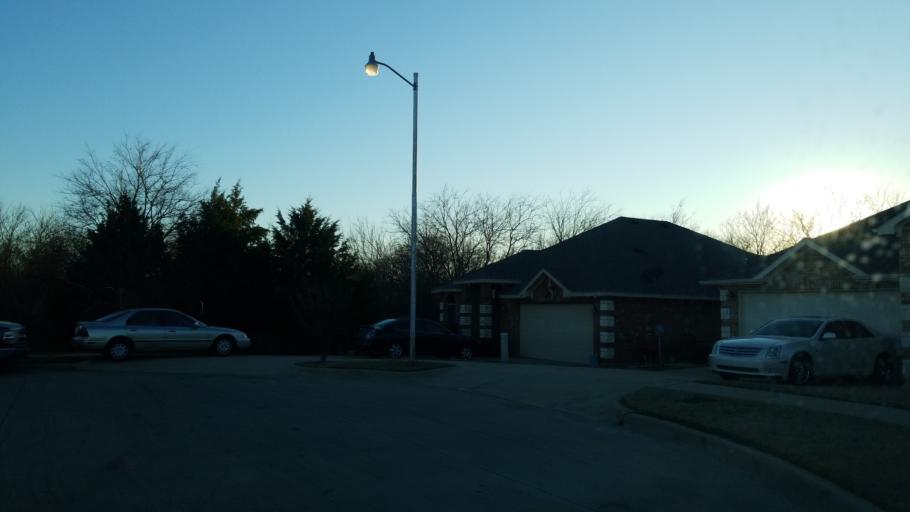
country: US
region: Texas
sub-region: Tarrant County
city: Arlington
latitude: 32.7267
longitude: -97.0547
